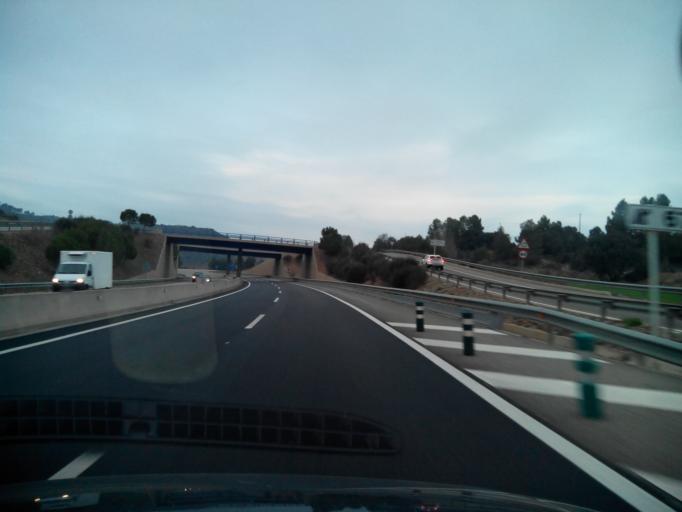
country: ES
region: Catalonia
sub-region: Provincia de Barcelona
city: Balsareny
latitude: 41.8525
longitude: 1.8789
